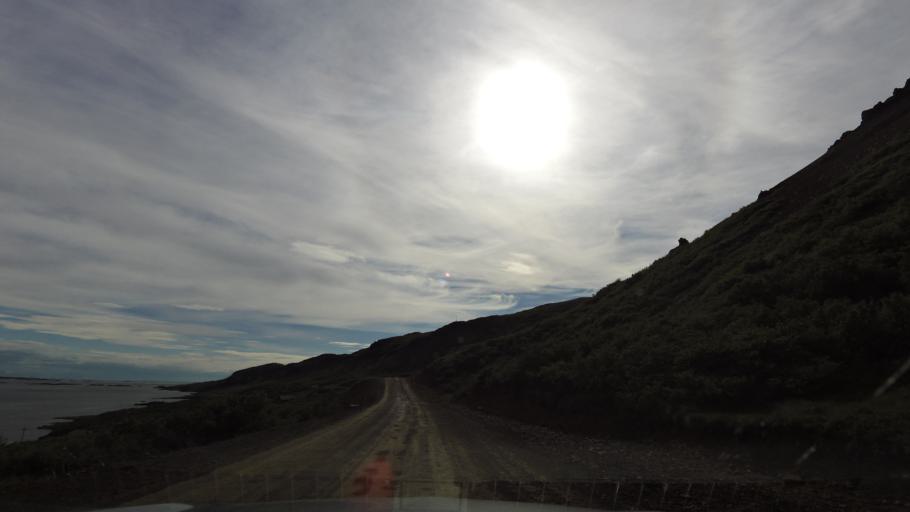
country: IS
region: West
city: Stykkisholmur
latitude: 65.5571
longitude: -22.3271
